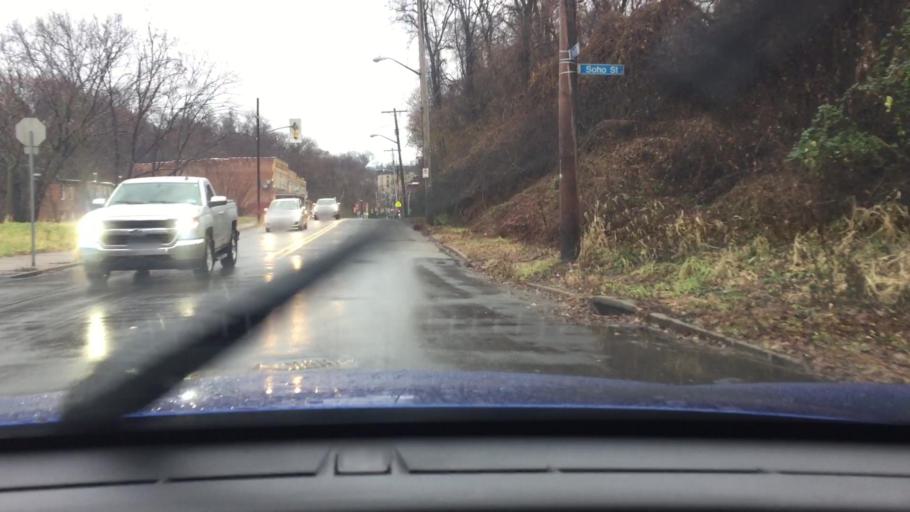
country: US
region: Pennsylvania
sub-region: Allegheny County
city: Pittsburgh
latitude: 40.4444
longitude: -79.9735
